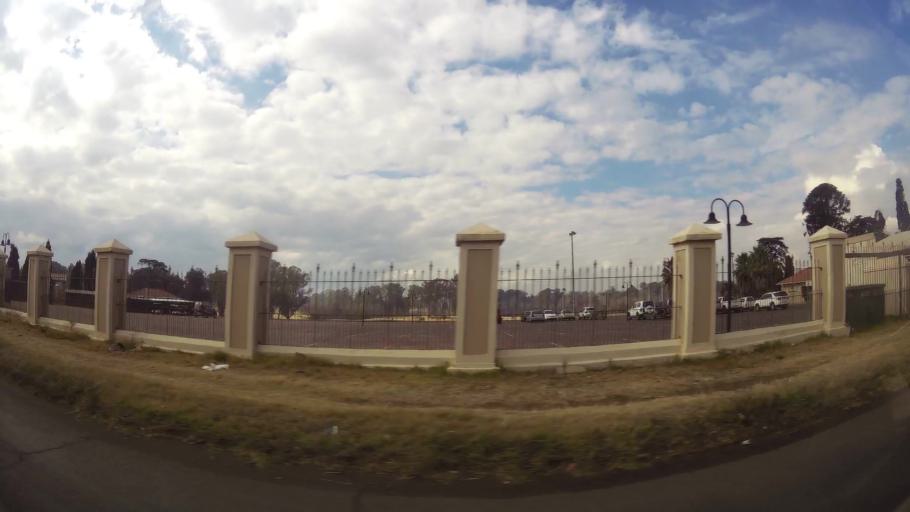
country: ZA
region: Gauteng
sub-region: Sedibeng District Municipality
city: Vereeniging
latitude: -26.6724
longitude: 27.9388
